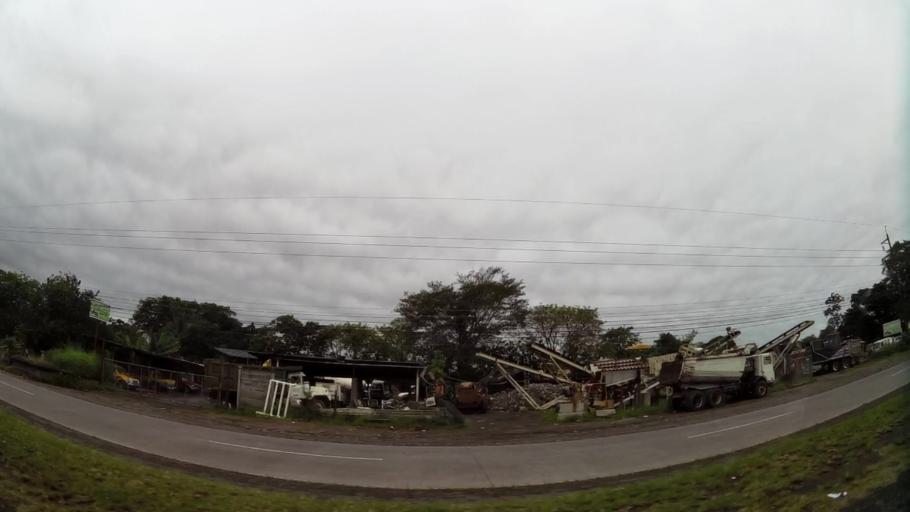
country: PA
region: Chiriqui
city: Tijera
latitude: 8.4744
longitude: -82.5471
